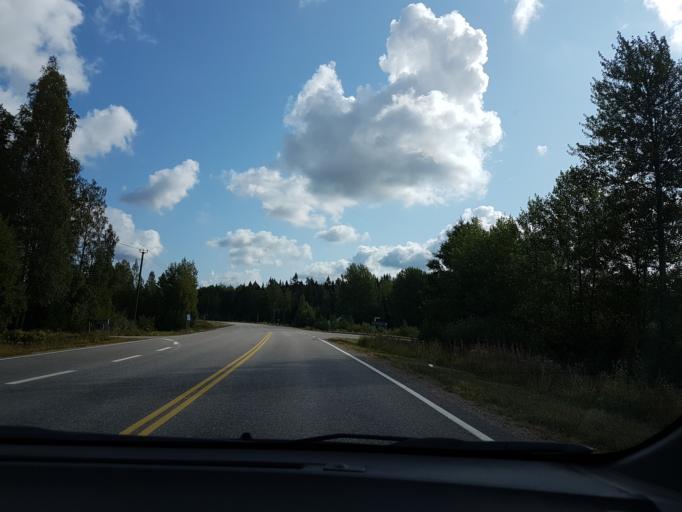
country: FI
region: Uusimaa
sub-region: Helsinki
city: Nickby
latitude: 60.4672
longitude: 25.2882
